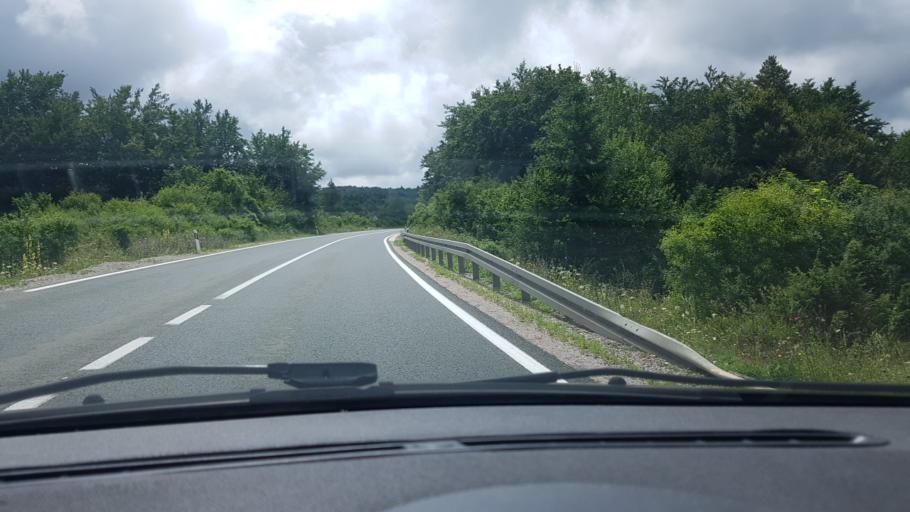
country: HR
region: Licko-Senjska
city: Jezerce
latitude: 44.8455
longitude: 15.6827
